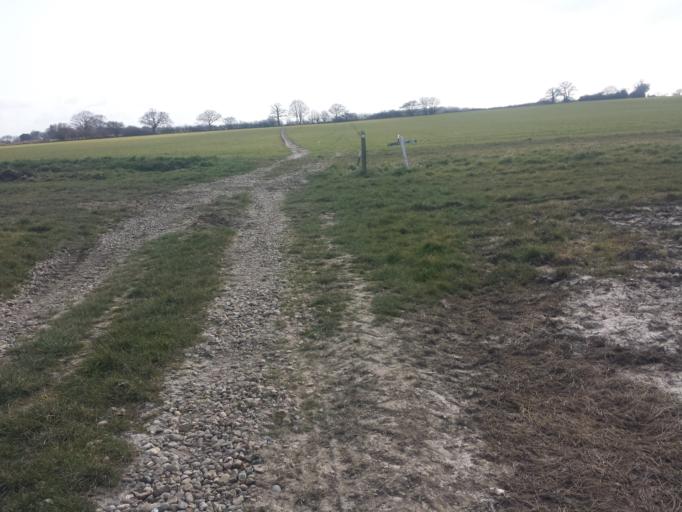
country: GB
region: England
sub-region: Essex
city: Mistley
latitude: 51.9056
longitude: 1.1523
